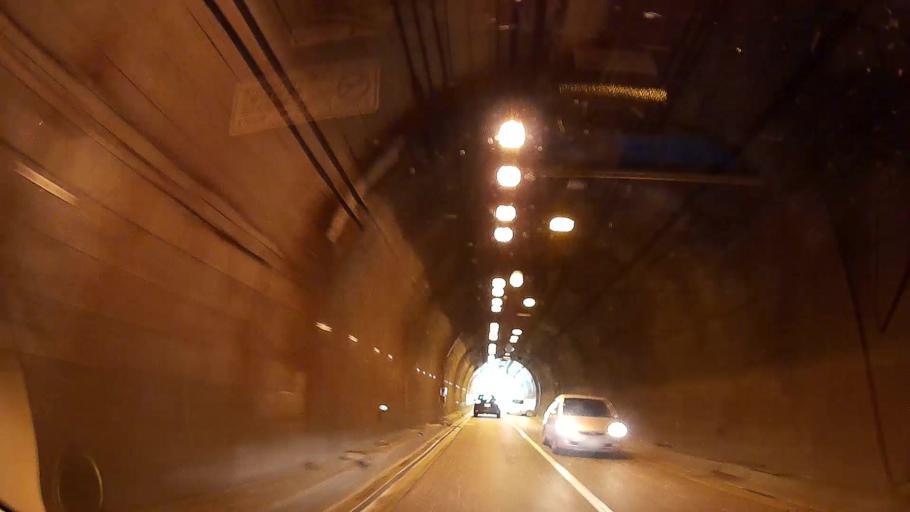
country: JP
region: Nagano
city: Toyoshina
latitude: 36.1513
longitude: 137.6848
